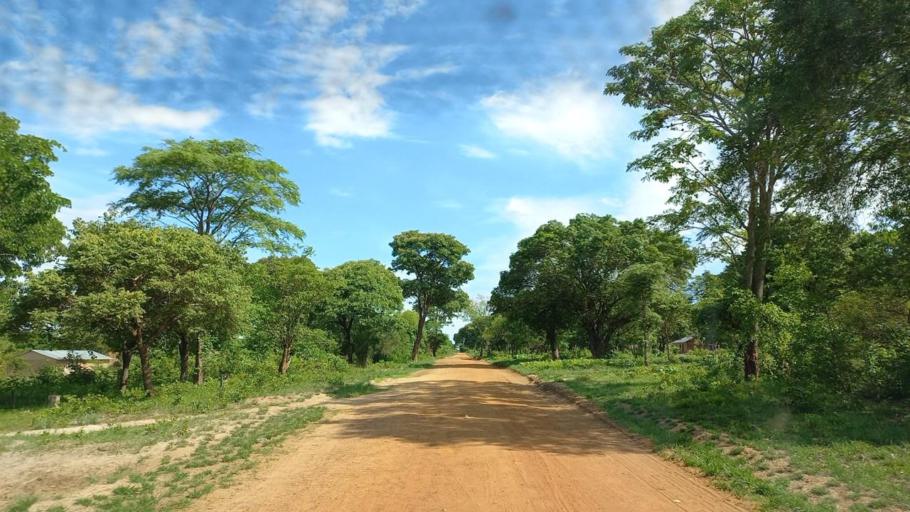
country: ZM
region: North-Western
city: Kabompo
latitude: -13.0689
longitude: 24.2183
